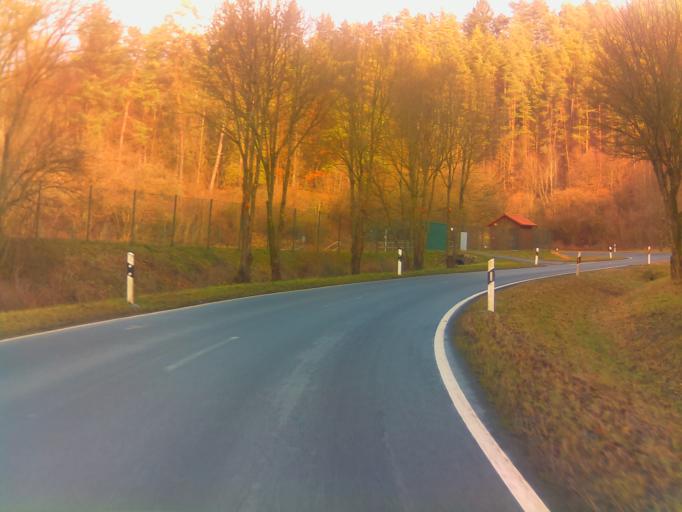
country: DE
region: Thuringia
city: Utendorf
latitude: 50.6006
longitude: 10.4421
